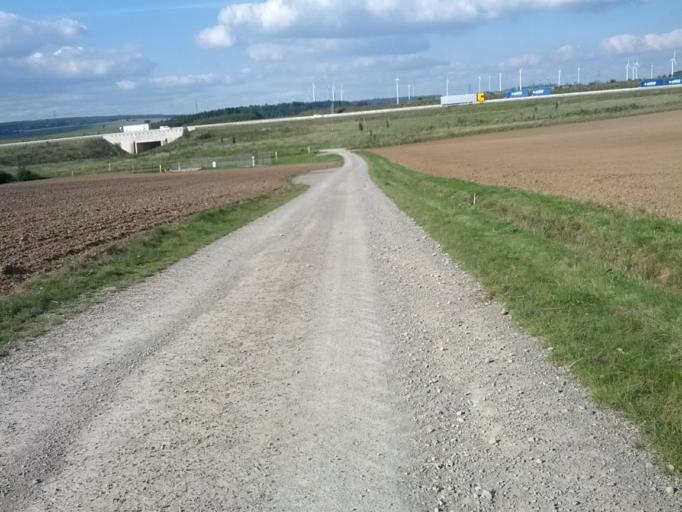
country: DE
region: Thuringia
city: Eisenach
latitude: 51.0125
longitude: 10.3273
